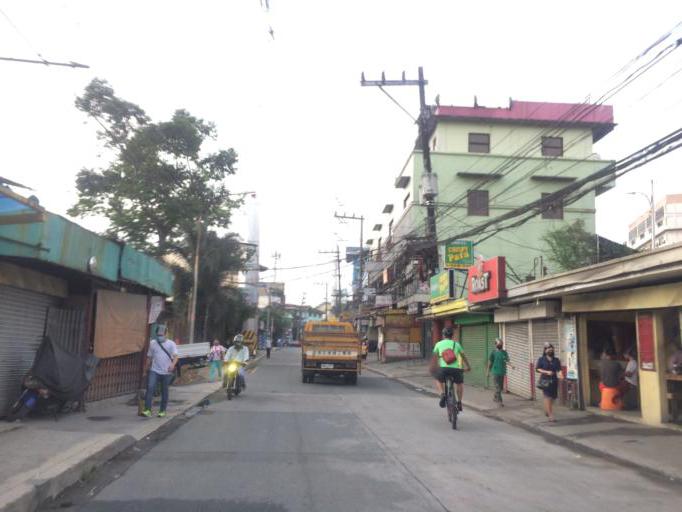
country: PH
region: Calabarzon
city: Del Monte
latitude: 14.6565
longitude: 121.0112
